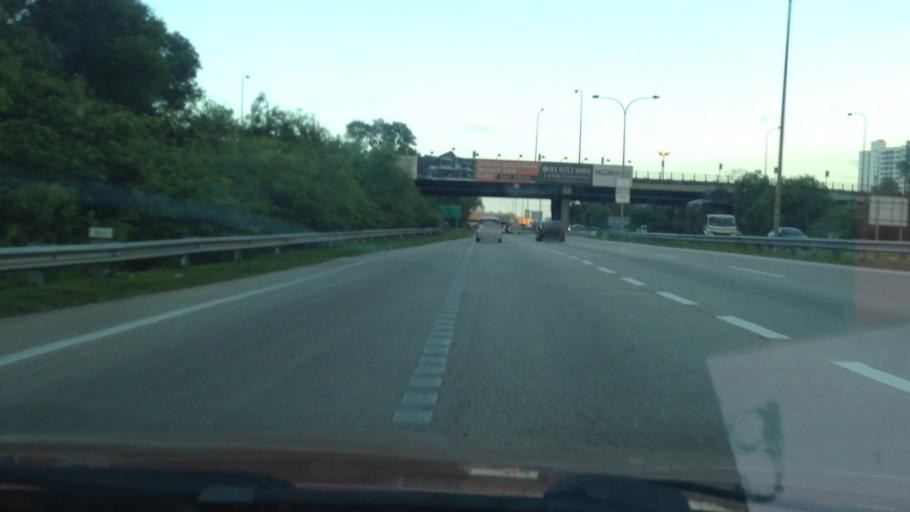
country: MY
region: Selangor
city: Shah Alam
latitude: 3.0955
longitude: 101.5492
